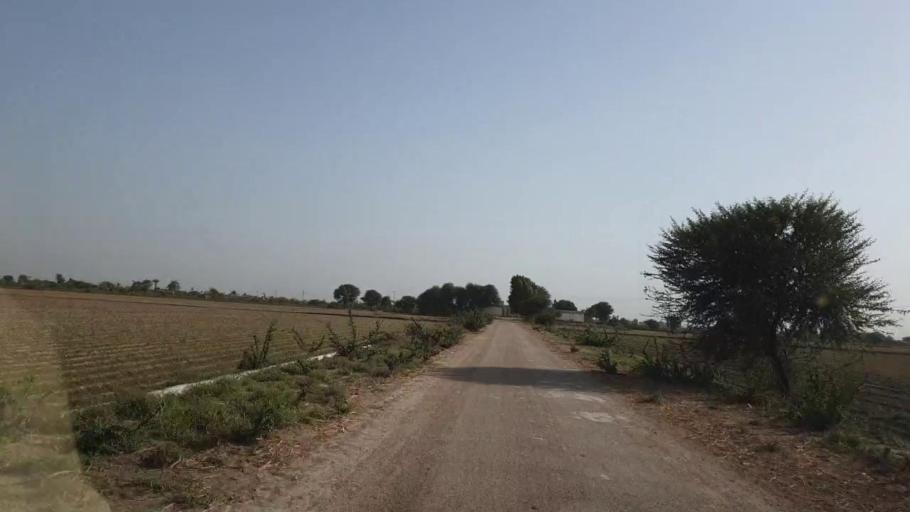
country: PK
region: Sindh
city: Tando Ghulam Ali
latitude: 25.0876
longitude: 68.8530
